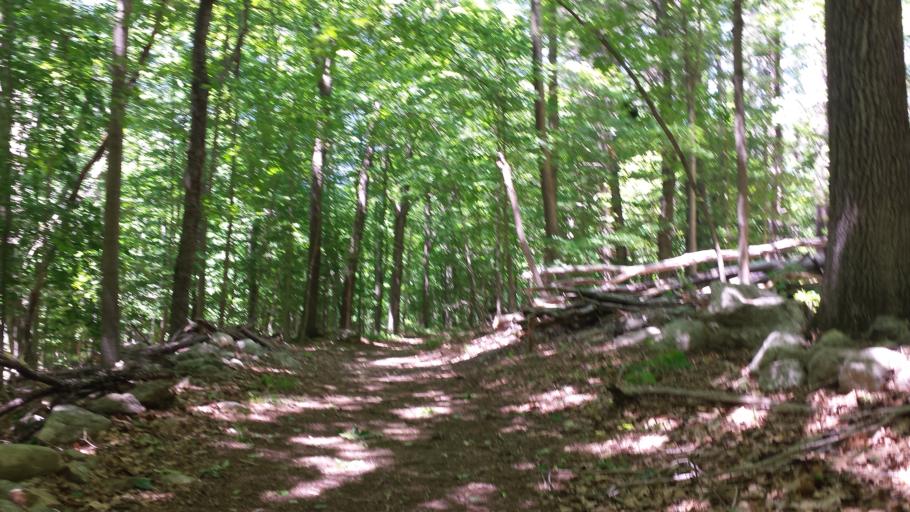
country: US
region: New York
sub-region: Westchester County
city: Pound Ridge
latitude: 41.2547
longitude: -73.5870
